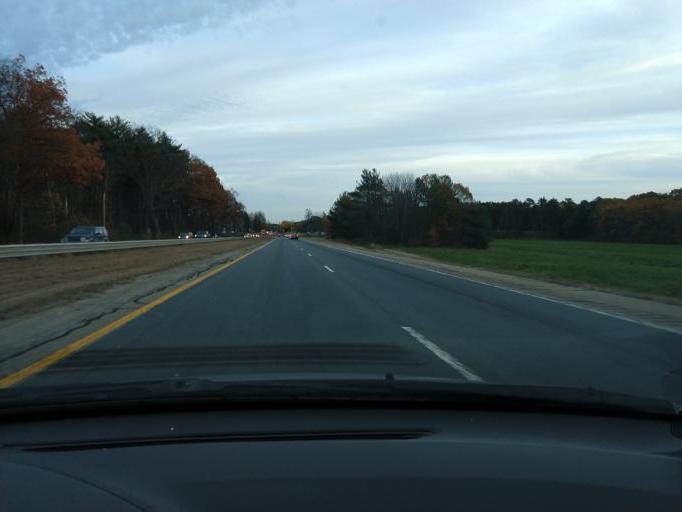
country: US
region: Massachusetts
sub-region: Middlesex County
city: West Concord
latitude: 42.4683
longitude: -71.4032
